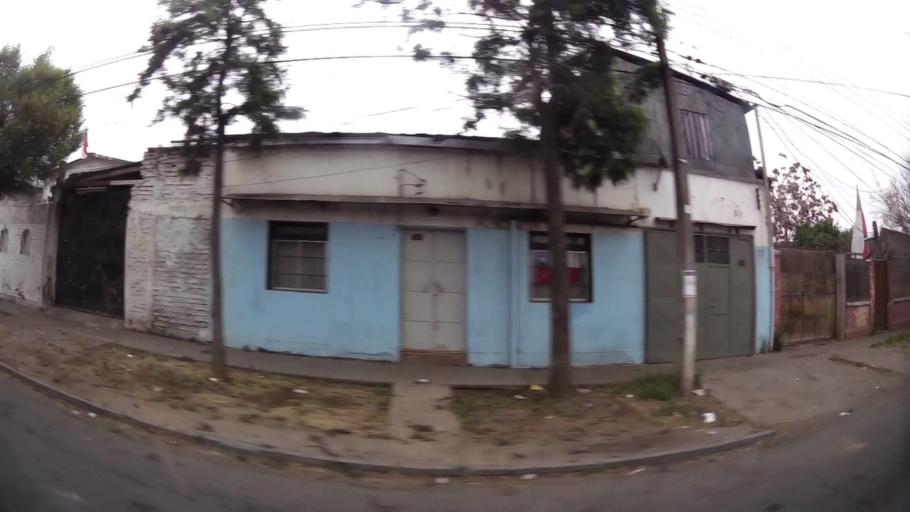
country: CL
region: Santiago Metropolitan
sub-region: Provincia de Santiago
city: Santiago
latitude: -33.4975
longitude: -70.6410
